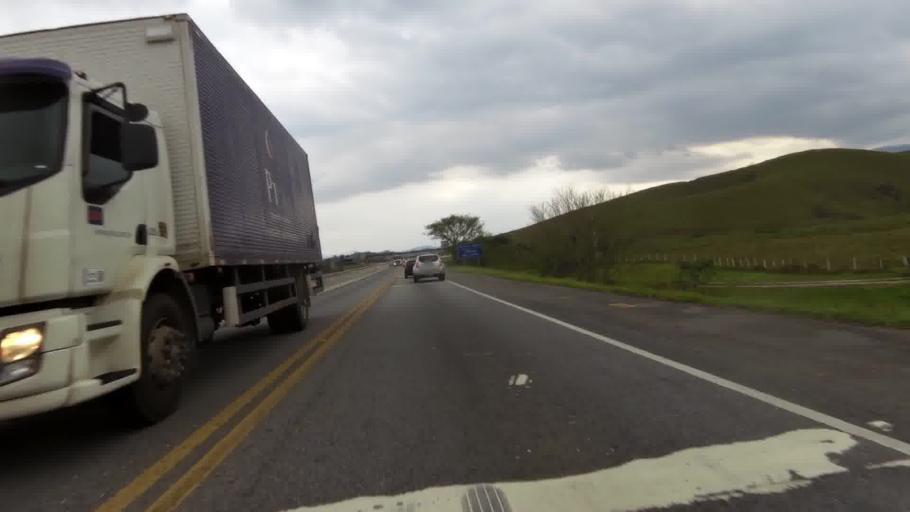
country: BR
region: Rio de Janeiro
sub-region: Rio Bonito
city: Rio Bonito
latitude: -22.6840
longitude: -42.5365
